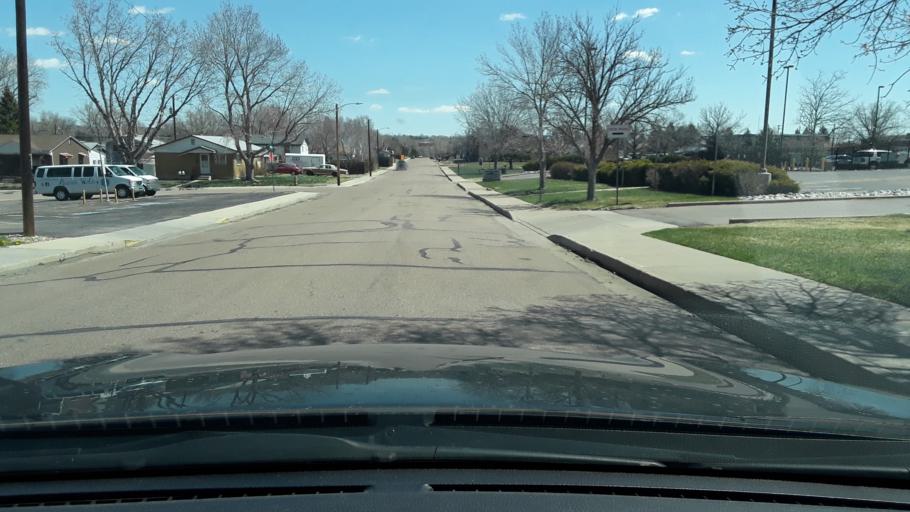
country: US
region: Colorado
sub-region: El Paso County
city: Colorado Springs
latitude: 38.8435
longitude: -104.7754
